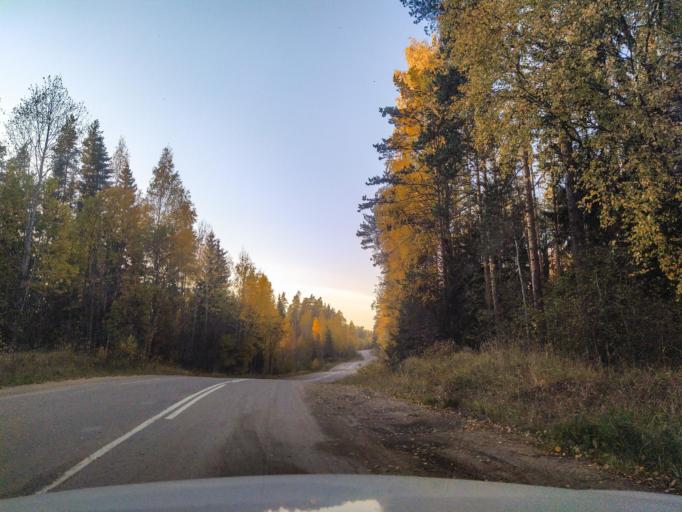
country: RU
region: Republic of Karelia
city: Lakhdenpokh'ya
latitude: 61.3783
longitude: 29.9737
